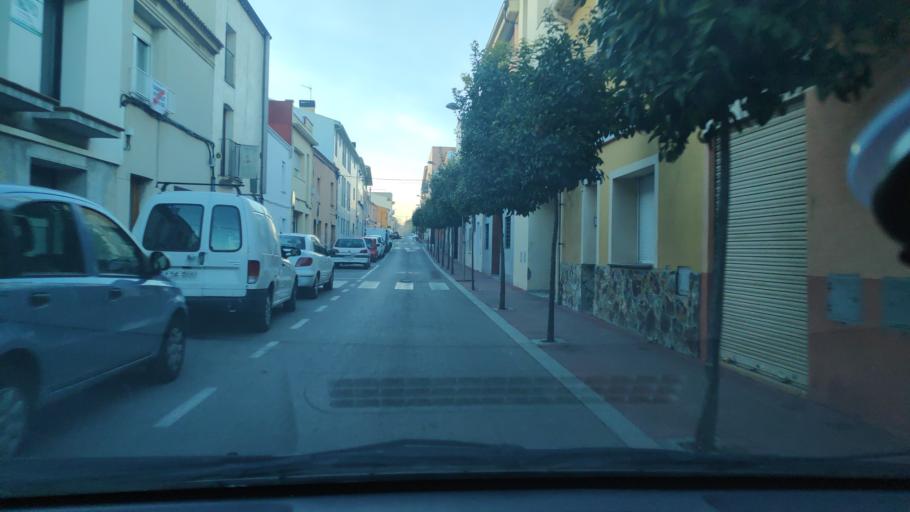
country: ES
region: Catalonia
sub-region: Provincia de Barcelona
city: Sant Quirze del Valles
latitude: 41.5339
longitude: 2.0796
